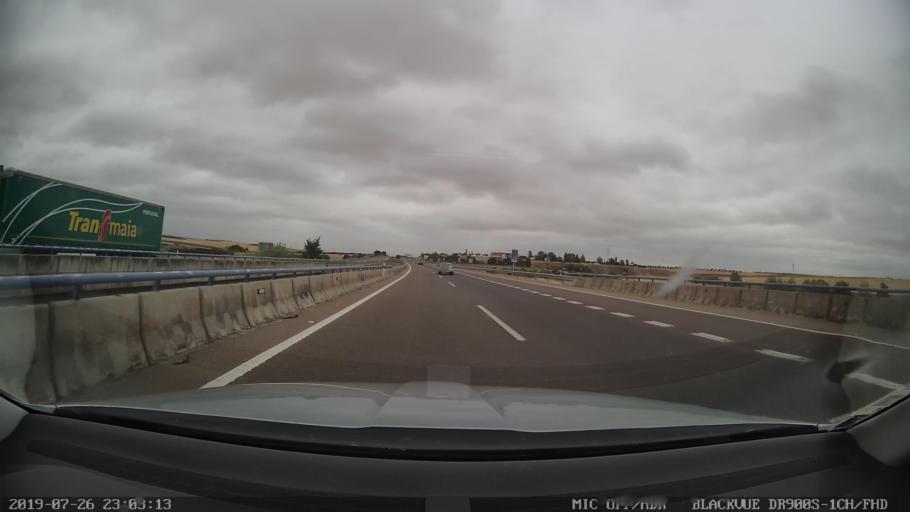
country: ES
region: Extremadura
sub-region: Provincia de Badajoz
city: Trujillanos
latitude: 38.9464
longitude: -6.2879
